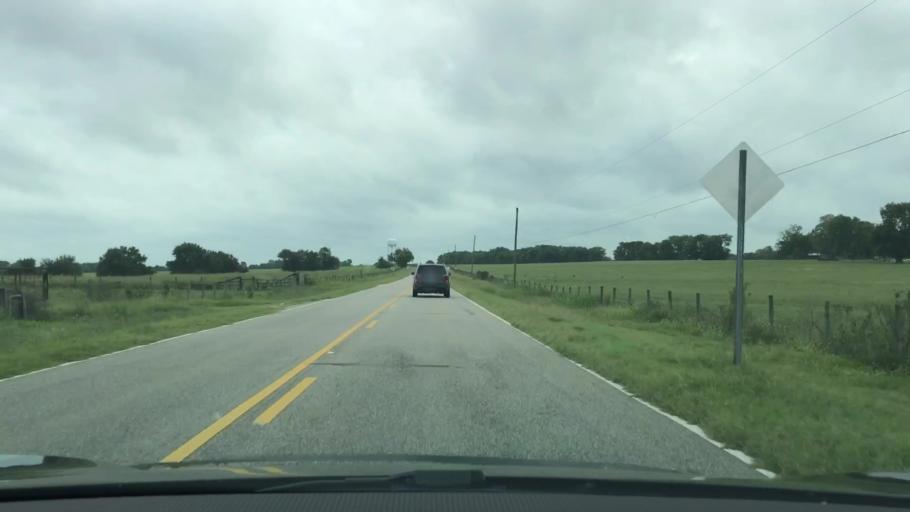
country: US
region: Alabama
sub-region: Montgomery County
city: Pike Road
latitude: 32.2832
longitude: -86.1008
